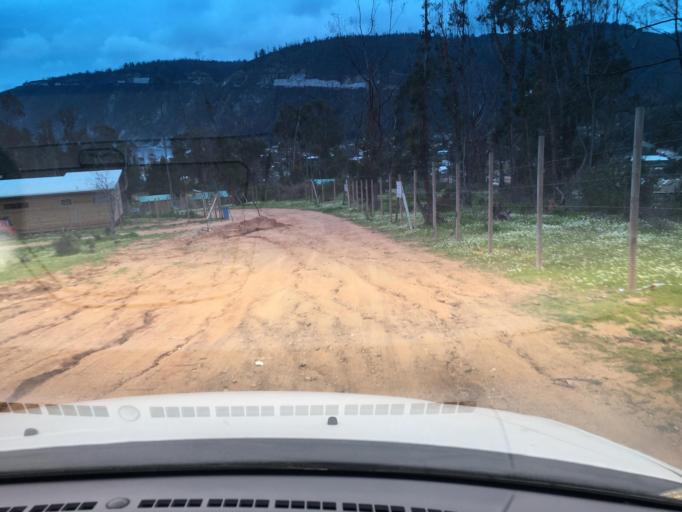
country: CL
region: Valparaiso
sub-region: Provincia de Valparaiso
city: Valparaiso
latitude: -33.1053
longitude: -71.6709
